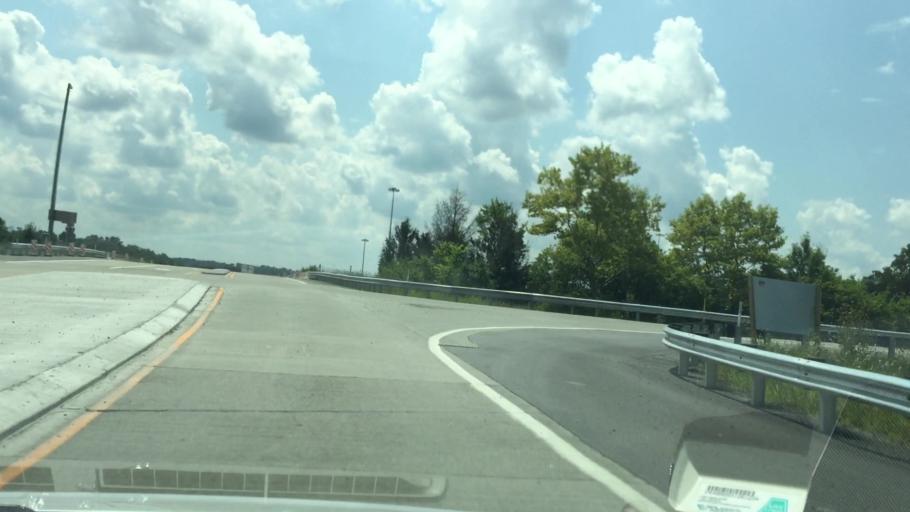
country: US
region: Pennsylvania
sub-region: Allegheny County
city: Enlow
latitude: 40.4732
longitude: -80.2227
